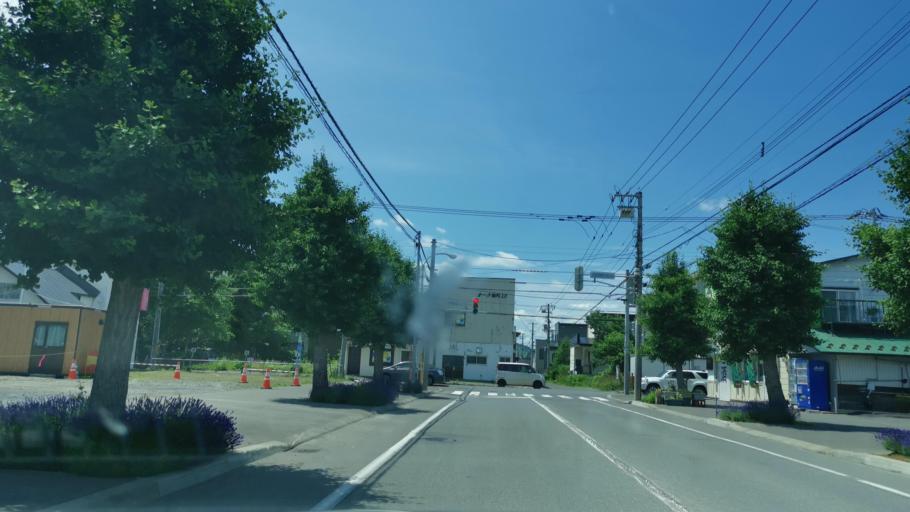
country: JP
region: Hokkaido
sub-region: Asahikawa-shi
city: Asahikawa
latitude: 43.7886
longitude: 142.3414
